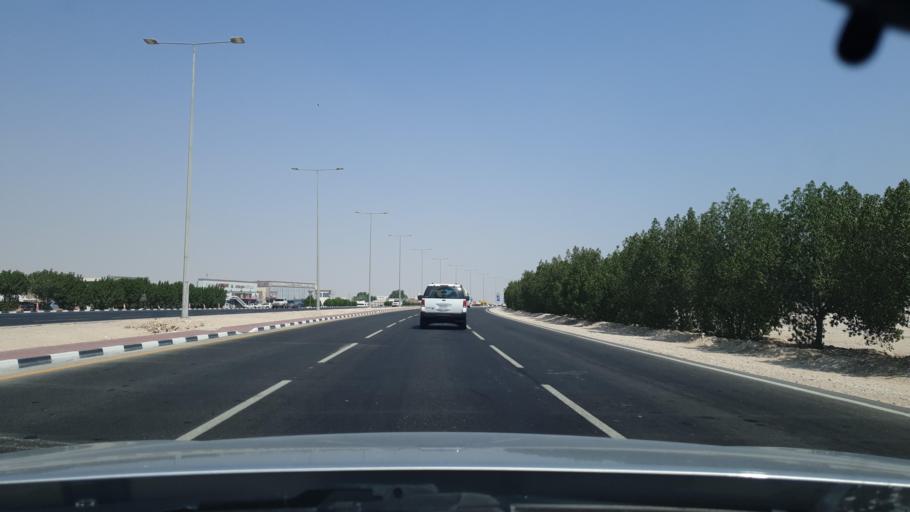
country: QA
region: Al Khawr
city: Al Khawr
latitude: 25.7097
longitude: 51.5059
